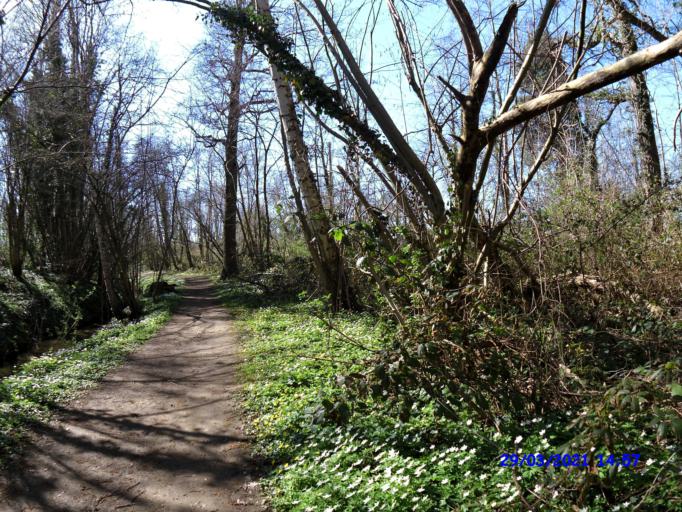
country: BE
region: Flanders
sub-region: Provincie Vlaams-Brabant
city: Lubbeek
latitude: 50.9076
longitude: 4.8516
